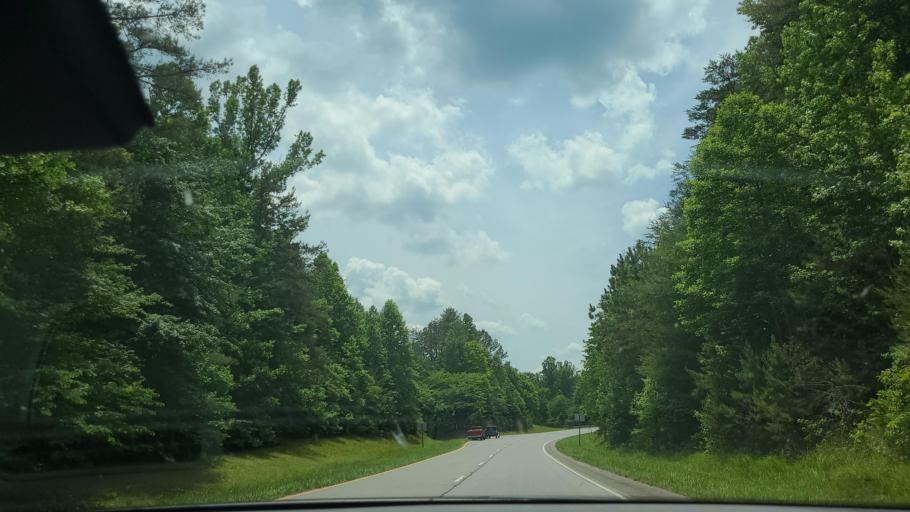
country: US
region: Georgia
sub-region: Fannin County
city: McCaysville
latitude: 35.0128
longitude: -84.2622
